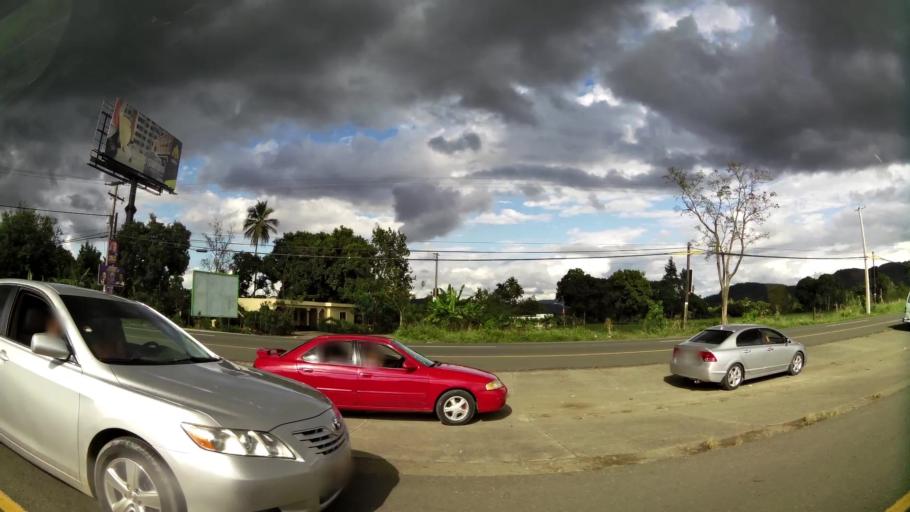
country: DO
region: Monsenor Nouel
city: Sabana del Puerto
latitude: 19.0020
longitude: -70.4384
